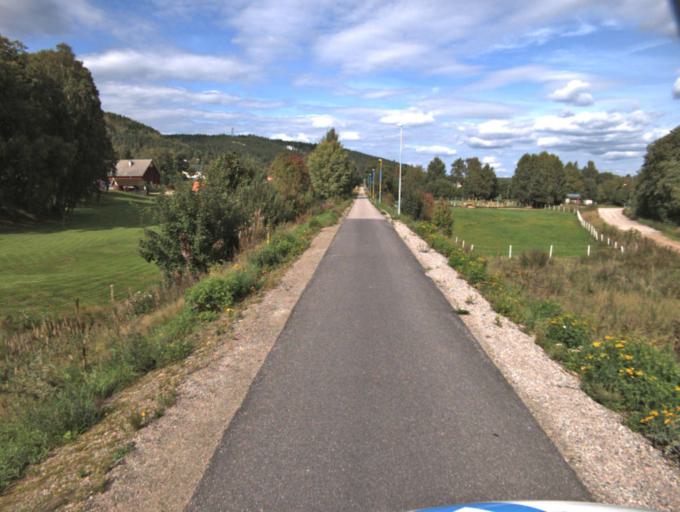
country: SE
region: Vaestra Goetaland
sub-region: Ulricehamns Kommun
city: Ulricehamn
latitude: 57.8116
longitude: 13.4120
